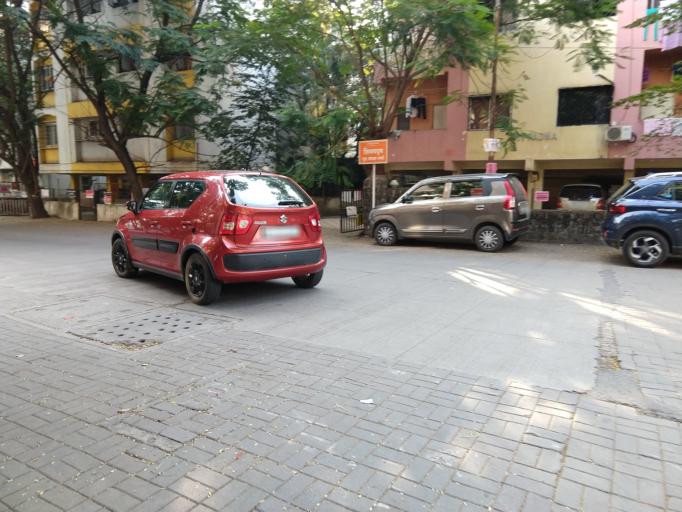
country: IN
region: Maharashtra
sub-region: Pune Division
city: Shivaji Nagar
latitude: 18.5095
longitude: 73.7905
